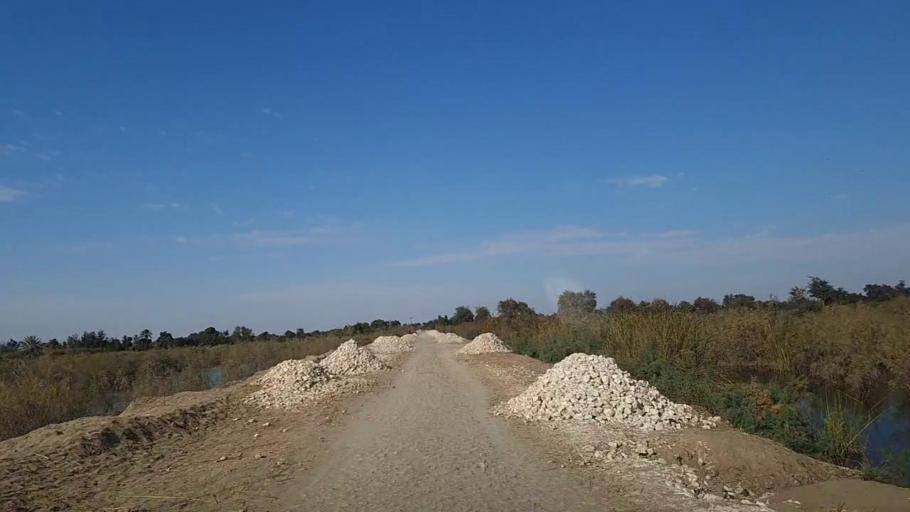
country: PK
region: Sindh
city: Khadro
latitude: 26.3027
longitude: 68.8141
